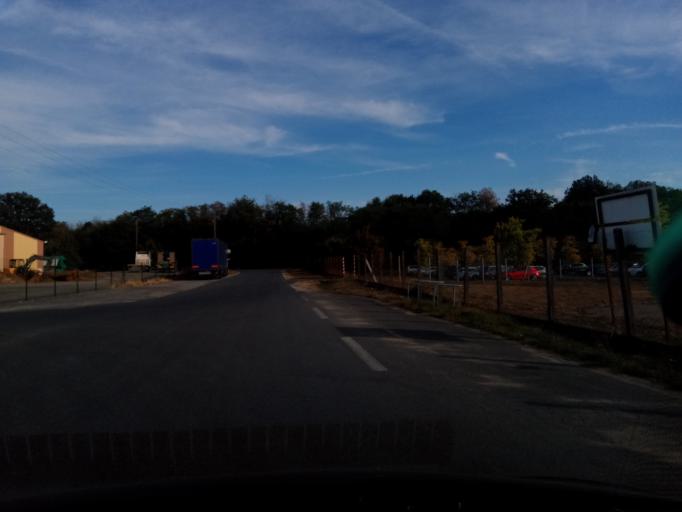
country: FR
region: Poitou-Charentes
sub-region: Departement de la Vienne
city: Saulge
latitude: 46.4019
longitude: 0.8908
